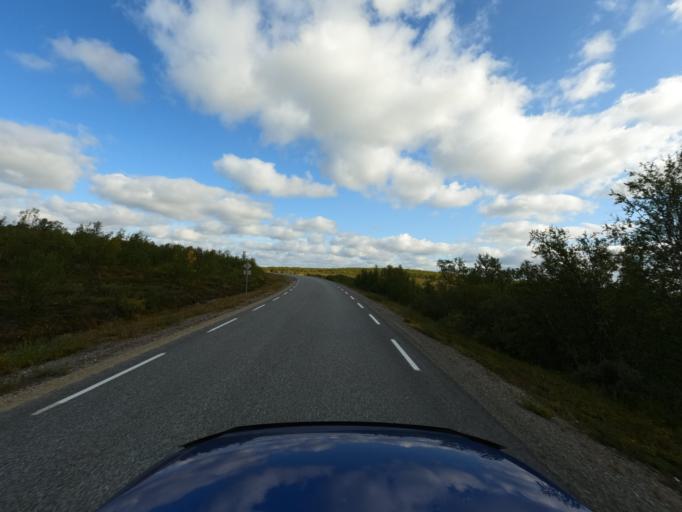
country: NO
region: Finnmark Fylke
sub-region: Porsanger
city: Lakselv
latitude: 69.3766
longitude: 24.4322
